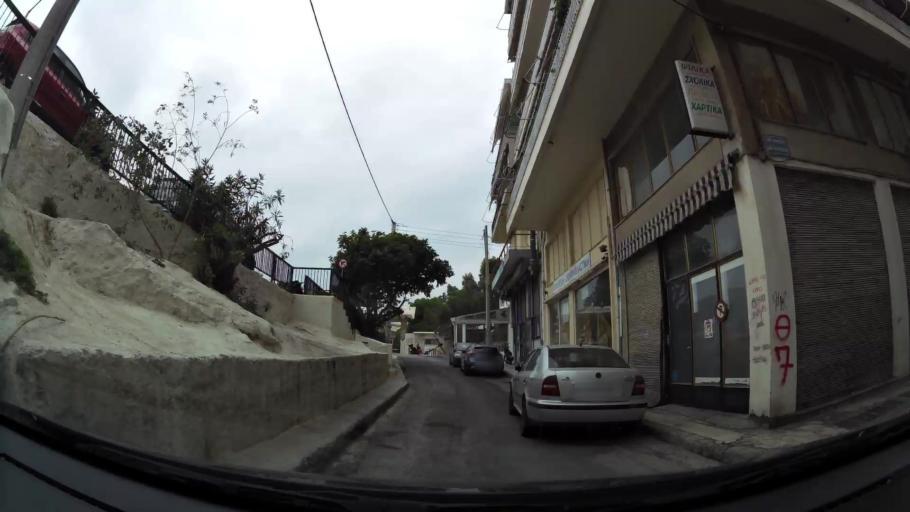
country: GR
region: Attica
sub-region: Nomos Attikis
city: Piraeus
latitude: 37.9348
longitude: 23.6296
